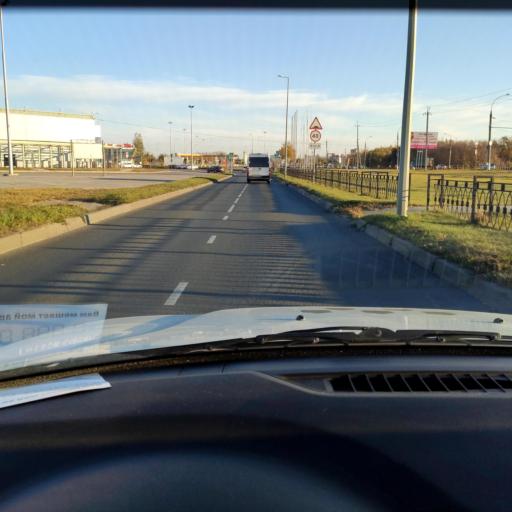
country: RU
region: Samara
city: Tol'yatti
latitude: 53.5438
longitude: 49.3836
